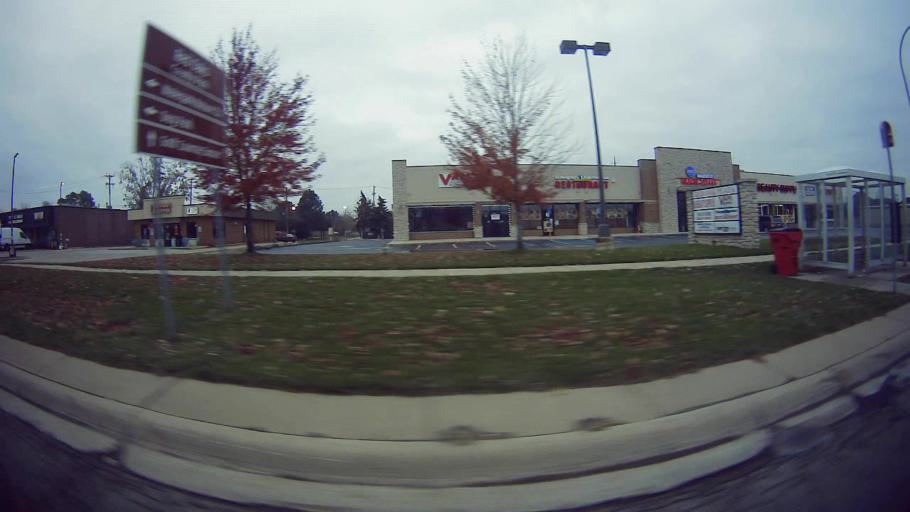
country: US
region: Michigan
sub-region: Oakland County
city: Madison Heights
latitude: 42.5211
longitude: -83.1066
